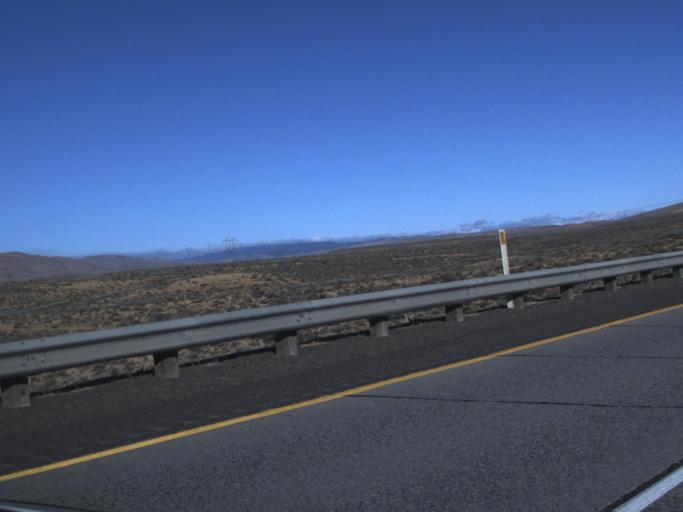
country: US
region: Washington
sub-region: Kittitas County
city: Kittitas
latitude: 46.8272
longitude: -120.3647
